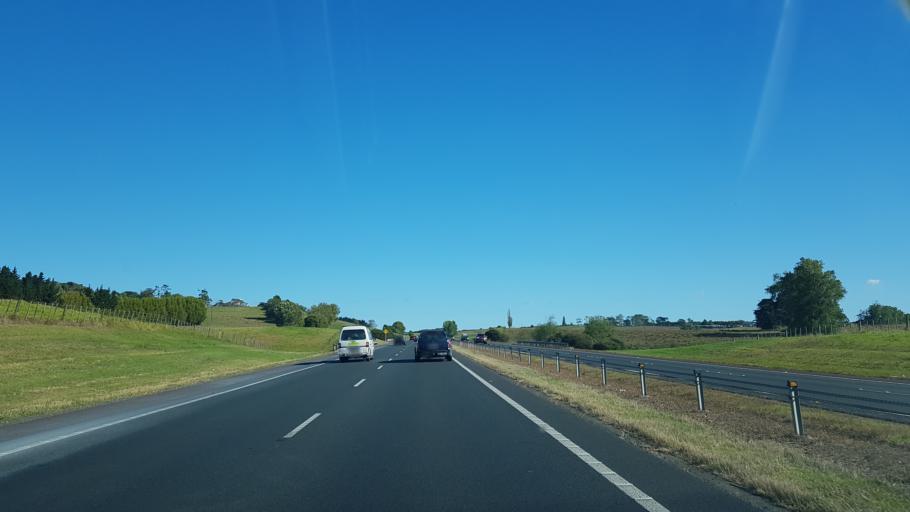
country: NZ
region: Auckland
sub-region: Auckland
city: Rothesay Bay
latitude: -36.6369
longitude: 174.6628
